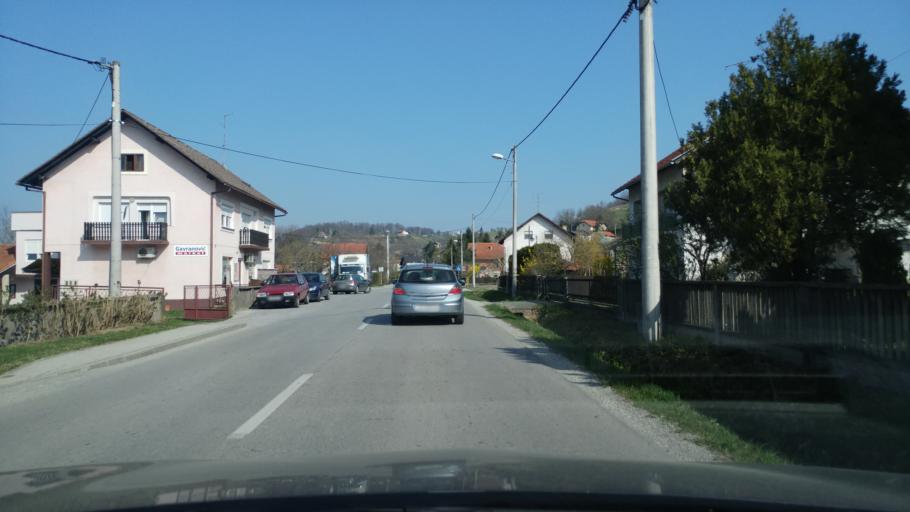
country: HR
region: Zagrebacka
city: Pojatno
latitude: 45.9105
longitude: 15.7800
